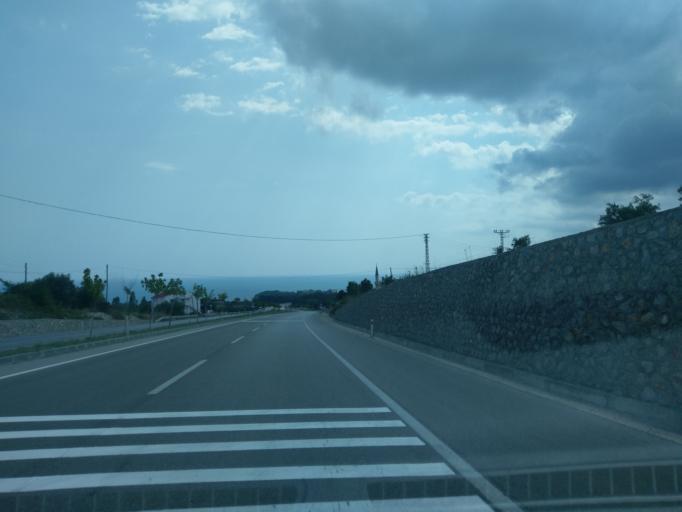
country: TR
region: Sinop
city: Kabali
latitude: 41.8486
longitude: 35.1277
